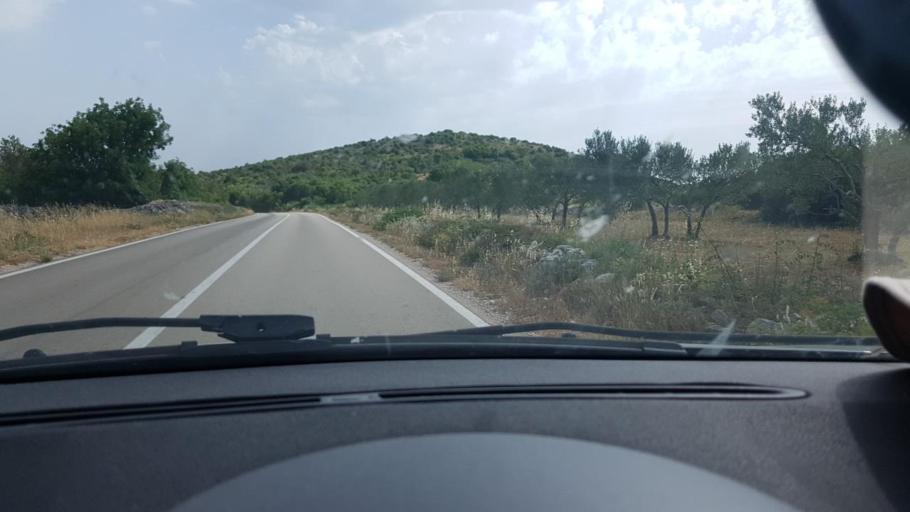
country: HR
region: Sibensko-Kniniska
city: Zaton
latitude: 43.8217
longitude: 15.7797
